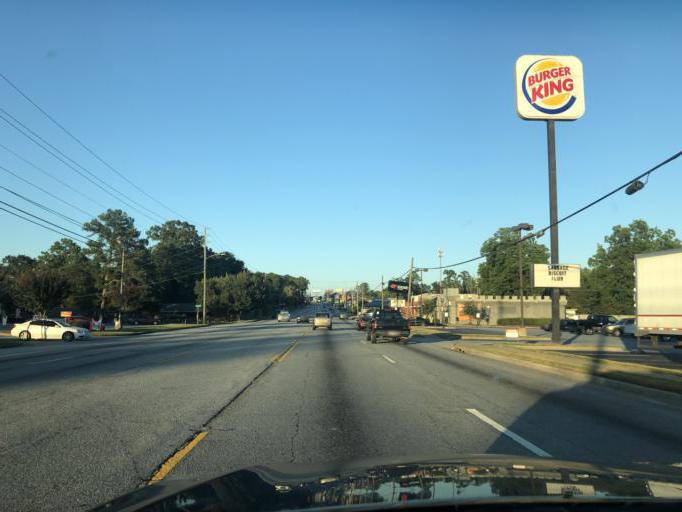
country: US
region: Georgia
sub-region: Muscogee County
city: Columbus
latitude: 32.4638
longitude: -84.9241
